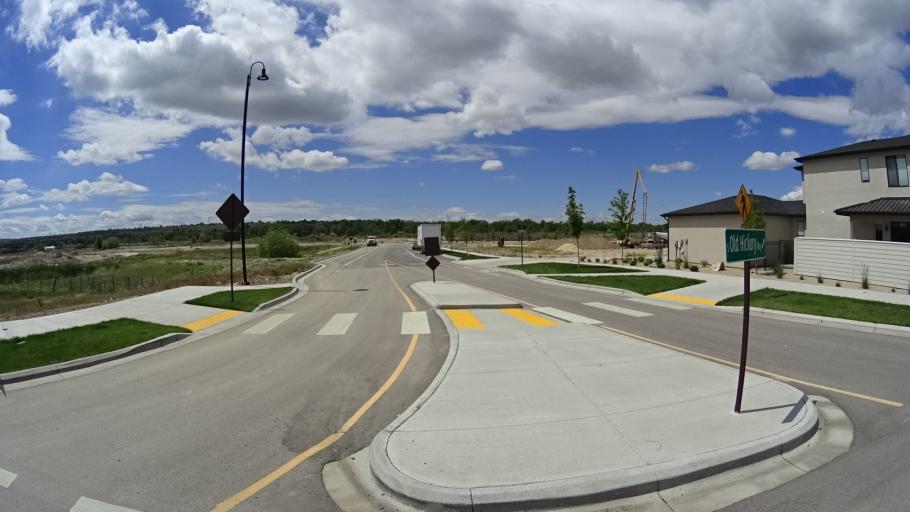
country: US
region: Idaho
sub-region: Ada County
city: Boise
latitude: 43.5743
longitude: -116.1338
